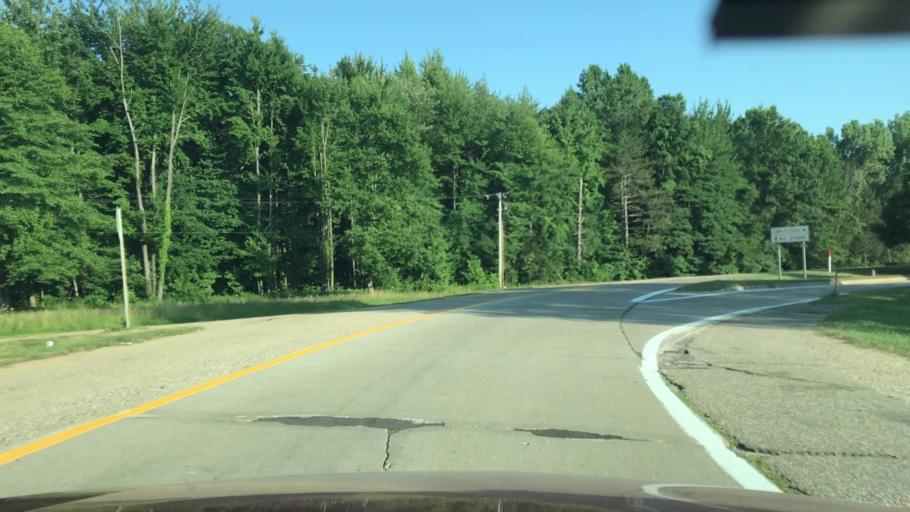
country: US
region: Michigan
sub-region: Berrien County
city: New Buffalo
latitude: 41.7667
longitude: -86.7383
